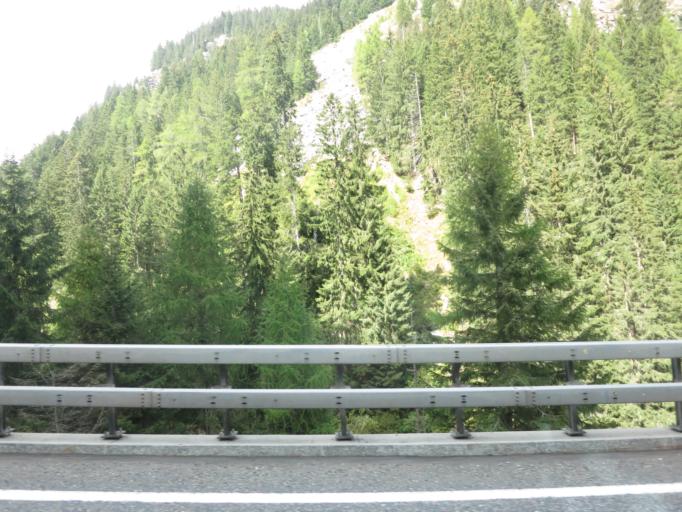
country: CH
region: Grisons
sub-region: Hinterrhein District
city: Thusis
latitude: 46.5665
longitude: 9.4039
